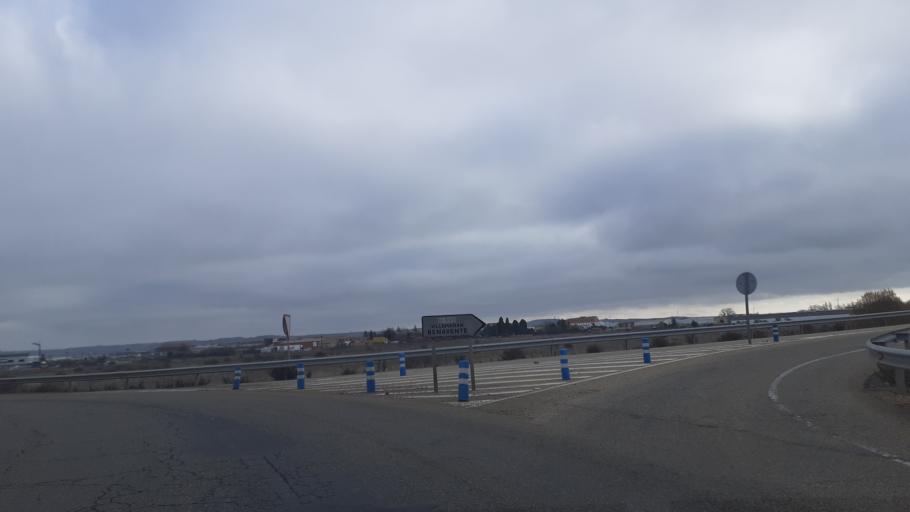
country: ES
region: Castille and Leon
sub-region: Provincia de Leon
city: Onzonilla
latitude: 42.5298
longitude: -5.5950
